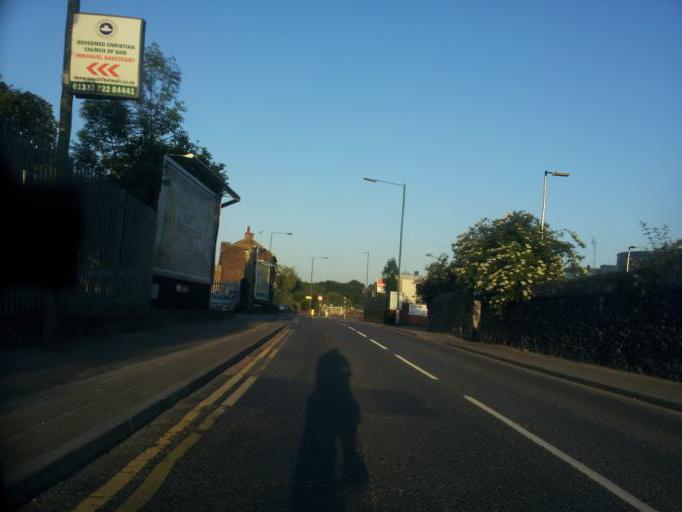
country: GB
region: England
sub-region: Kent
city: Dartford
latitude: 51.4489
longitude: 0.2168
